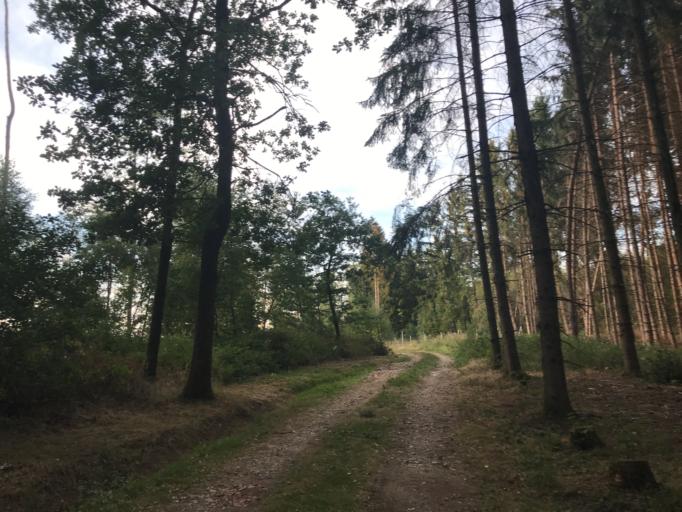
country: DE
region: Bavaria
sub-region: Upper Palatinate
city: Auerbach
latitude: 49.7159
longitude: 11.6337
